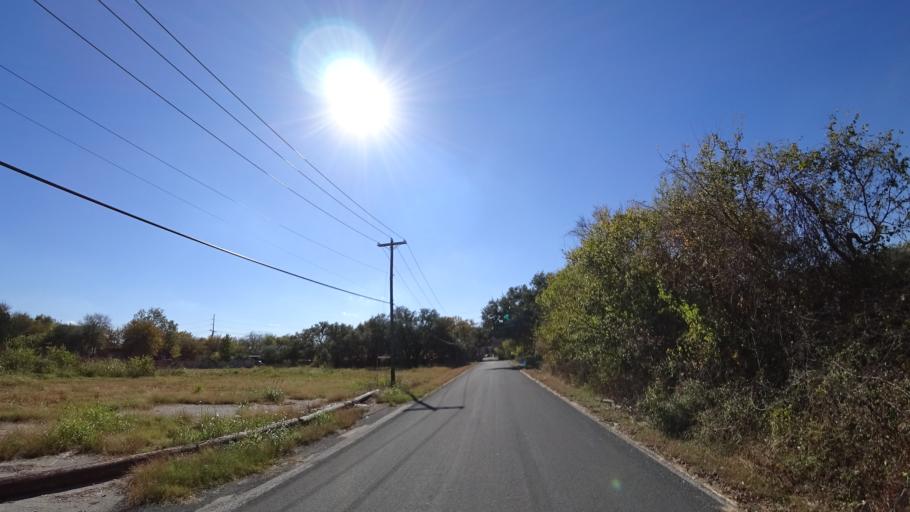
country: US
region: Texas
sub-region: Travis County
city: Wells Branch
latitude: 30.4368
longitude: -97.6932
